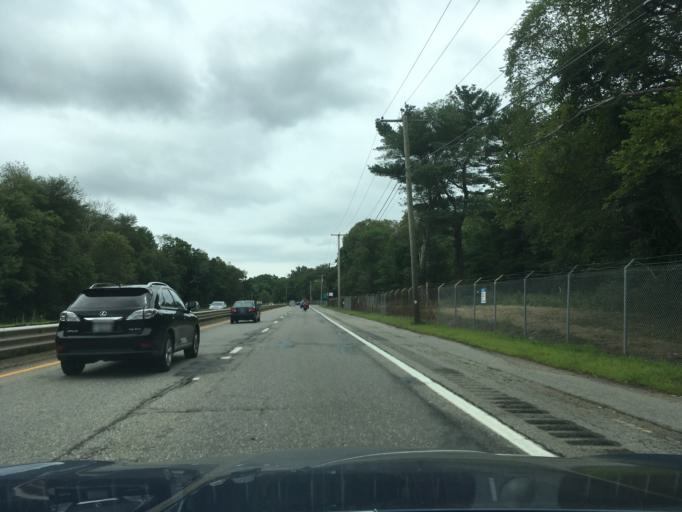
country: US
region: Massachusetts
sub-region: Bristol County
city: Seekonk
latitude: 41.7847
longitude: -71.3342
